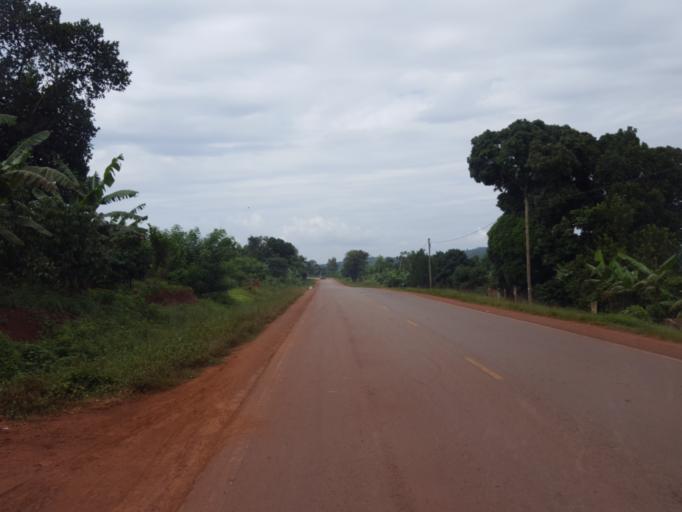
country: UG
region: Central Region
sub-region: Mityana District
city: Mityana
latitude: 0.6443
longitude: 32.0968
